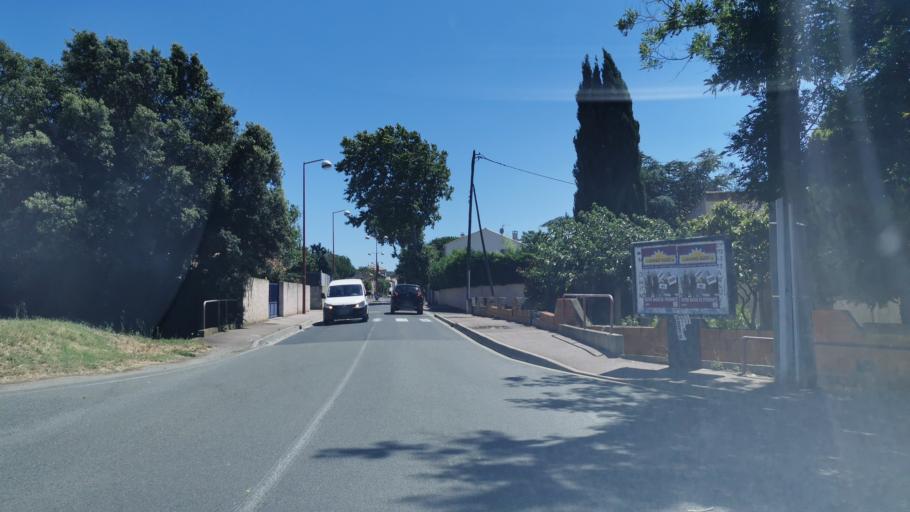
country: FR
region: Languedoc-Roussillon
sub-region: Departement de l'Aude
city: Vinassan
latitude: 43.2068
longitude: 3.0745
